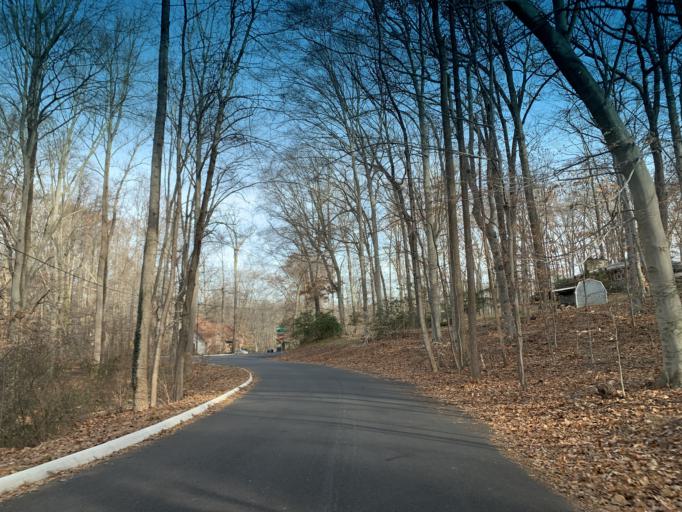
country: US
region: Maryland
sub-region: Harford County
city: South Bel Air
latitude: 39.5234
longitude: -76.3275
